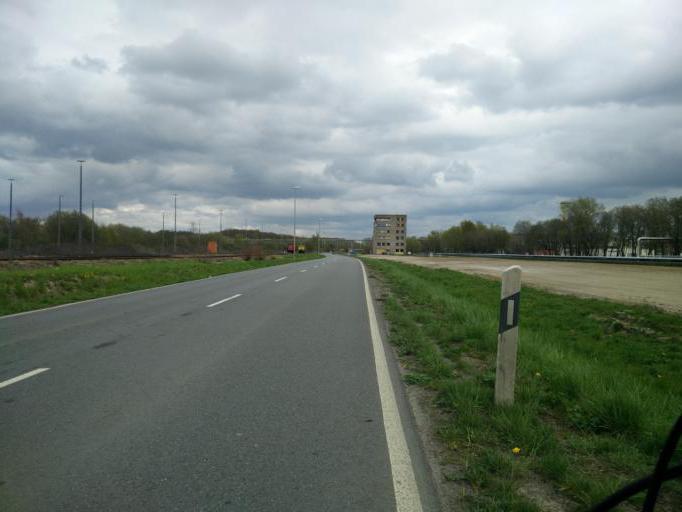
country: DE
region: Mecklenburg-Vorpommern
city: Nienhagen
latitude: 54.1463
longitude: 12.1417
